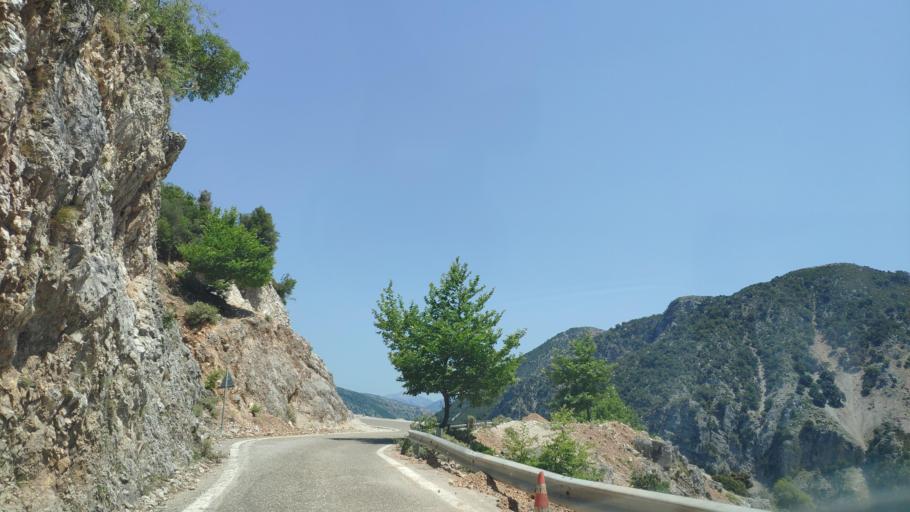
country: GR
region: West Greece
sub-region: Nomos Aitolias kai Akarnanias
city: Krikellos
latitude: 39.0126
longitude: 21.3727
